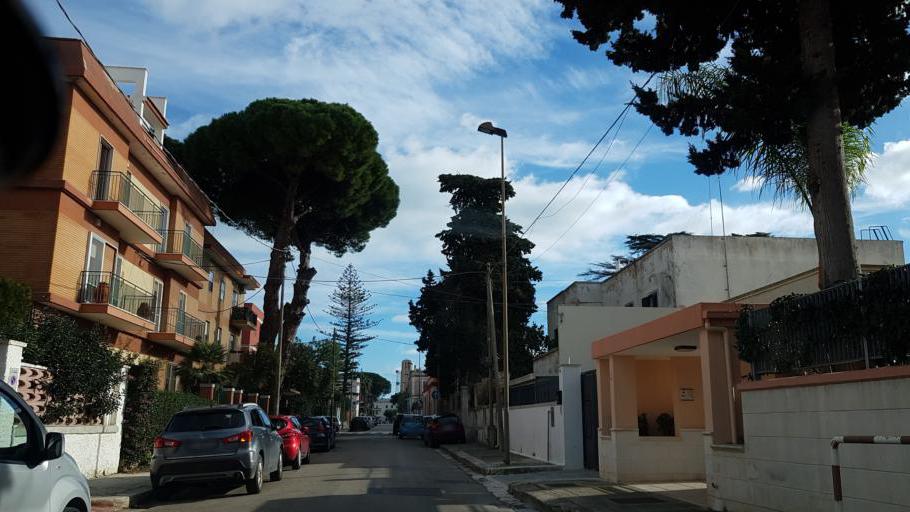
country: IT
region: Apulia
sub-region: Provincia di Brindisi
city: Brindisi
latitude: 40.6473
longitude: 17.9408
